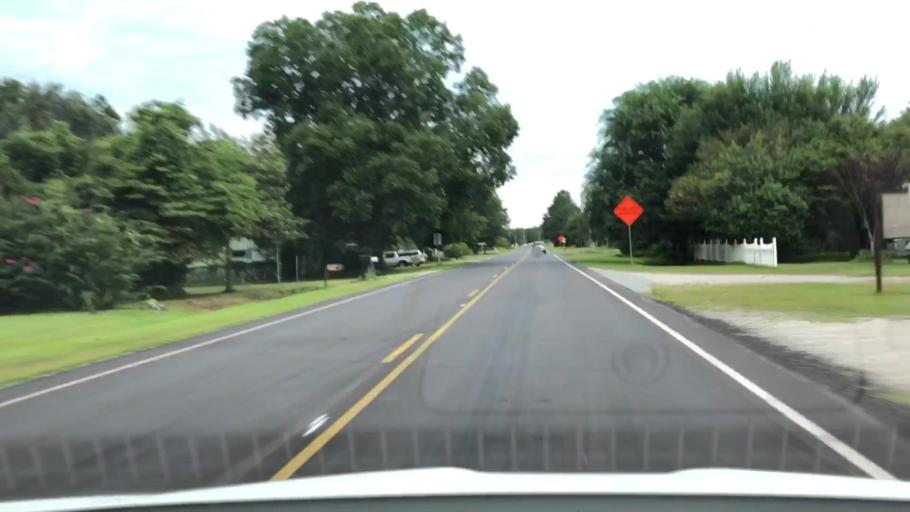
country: US
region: North Carolina
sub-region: Jones County
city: Maysville
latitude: 34.8793
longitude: -77.2050
